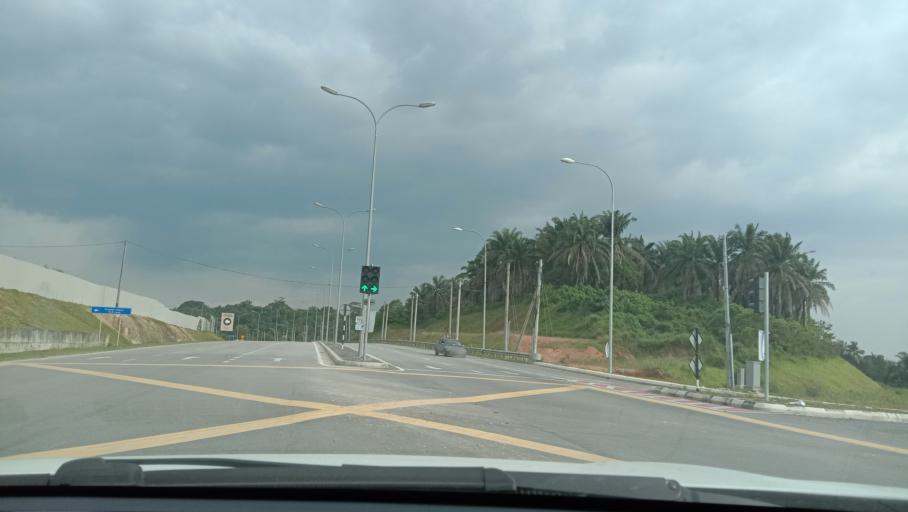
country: MY
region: Selangor
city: Ladang Seri Kundang
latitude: 3.2402
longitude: 101.4770
